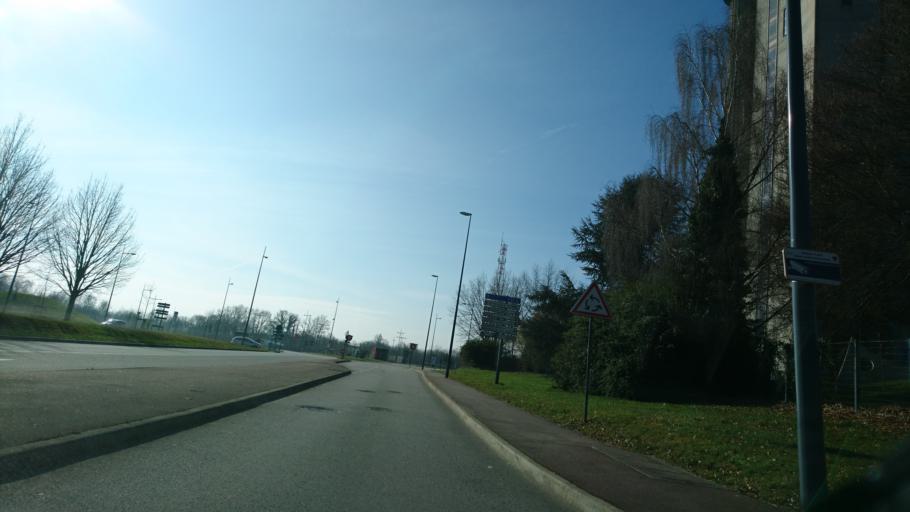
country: FR
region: Limousin
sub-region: Departement de la Haute-Vienne
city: Le Palais-sur-Vienne
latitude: 45.8726
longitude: 1.2998
